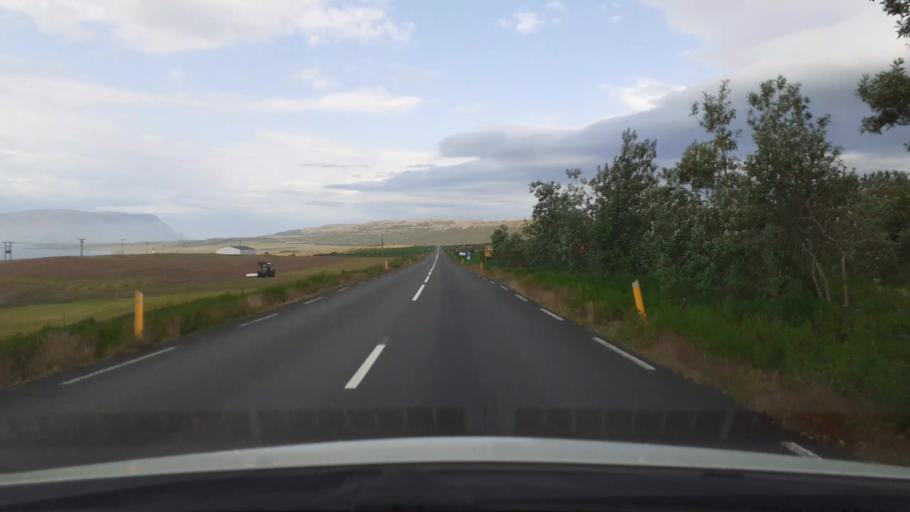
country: IS
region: Capital Region
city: Mosfellsbaer
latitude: 64.4102
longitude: -21.5997
